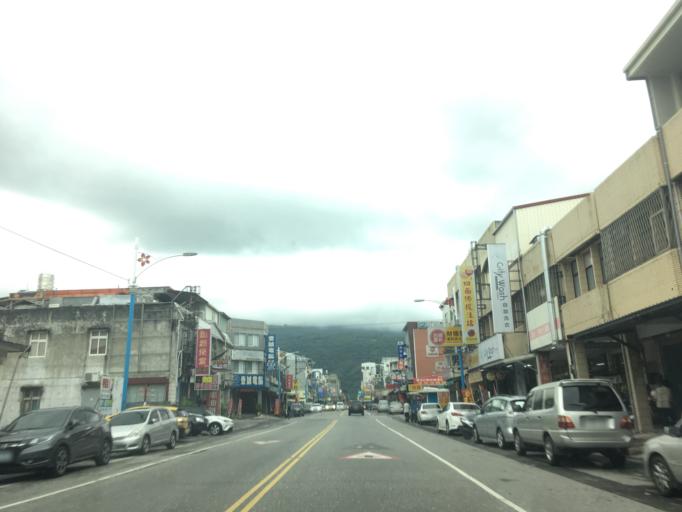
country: TW
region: Taiwan
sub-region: Hualien
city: Hualian
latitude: 23.9785
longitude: 121.5695
